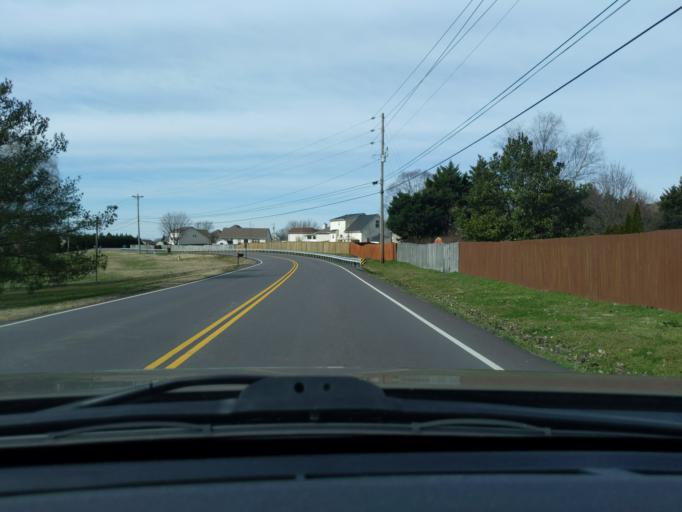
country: US
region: Tennessee
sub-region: Wilson County
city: Rural Hill
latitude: 36.1661
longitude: -86.4650
